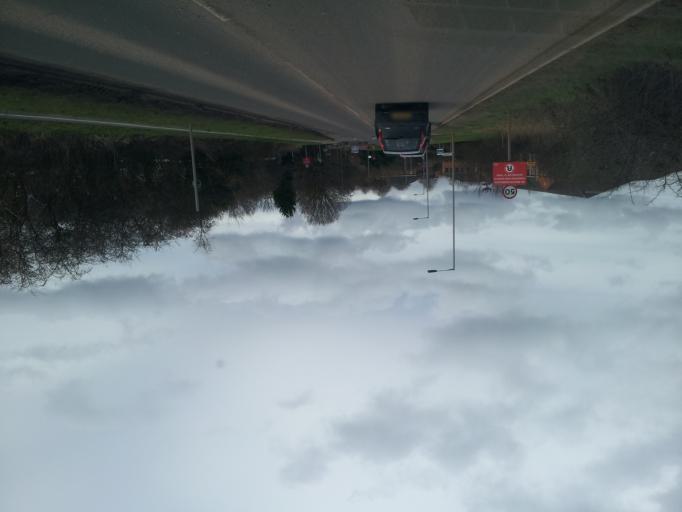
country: GB
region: England
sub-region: Staffordshire
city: Stafford
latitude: 52.8151
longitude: -2.0903
